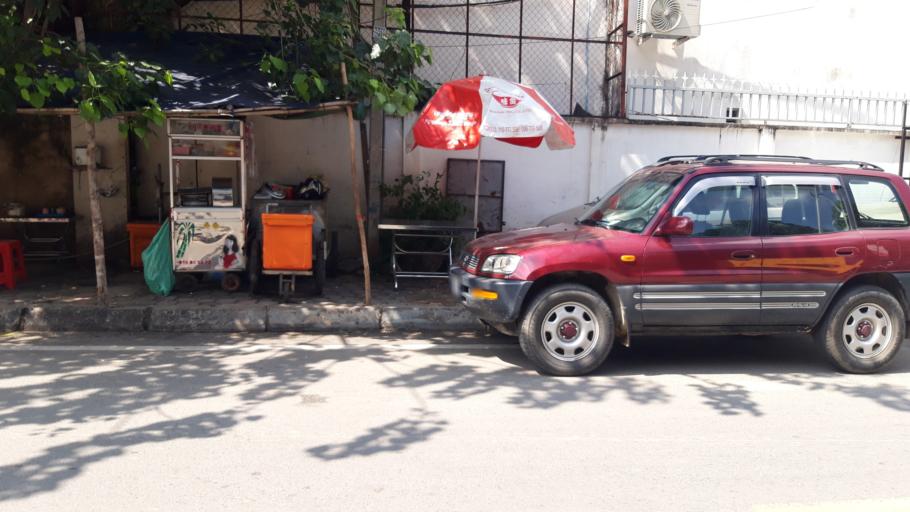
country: KH
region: Phnom Penh
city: Phnom Penh
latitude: 11.5520
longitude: 104.9281
